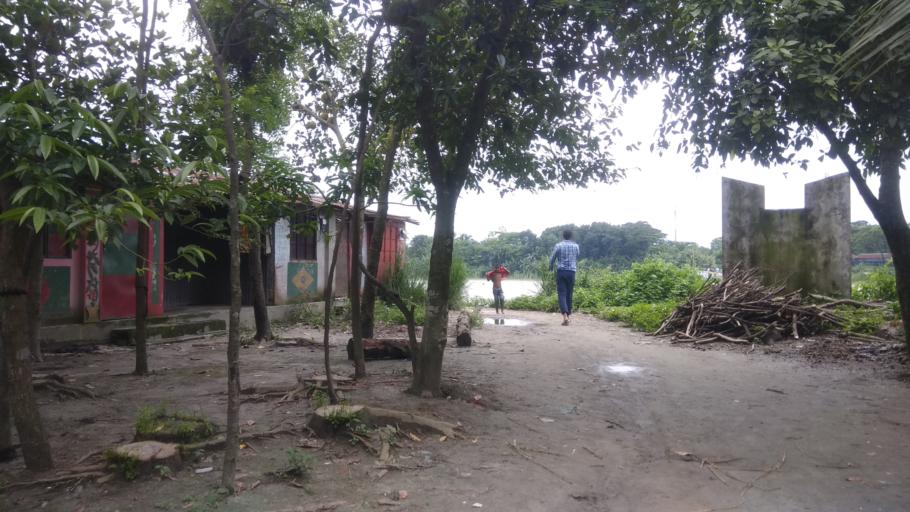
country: BD
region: Dhaka
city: Azimpur
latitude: 23.6724
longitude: 90.2871
